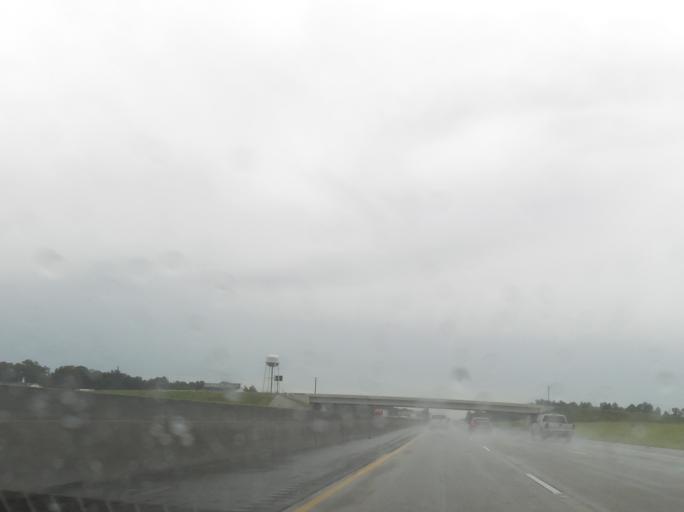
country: US
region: Georgia
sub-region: Tift County
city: Unionville
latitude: 31.3604
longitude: -83.4908
